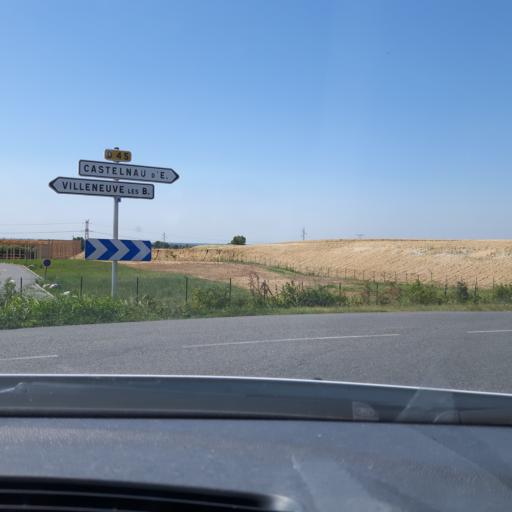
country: FR
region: Midi-Pyrenees
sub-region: Departement de la Haute-Garonne
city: Bouloc
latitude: 43.7704
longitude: 1.3878
